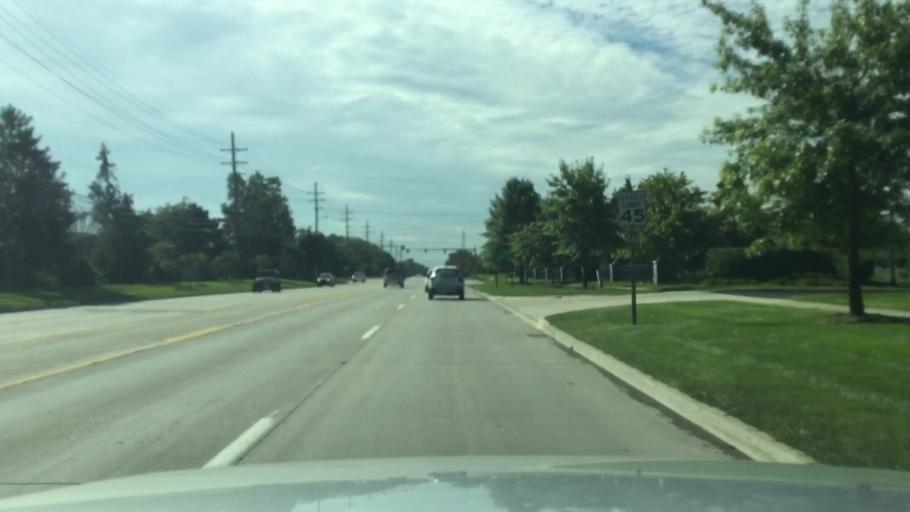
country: US
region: Michigan
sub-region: Wayne County
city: Canton
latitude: 42.3163
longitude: -83.4877
